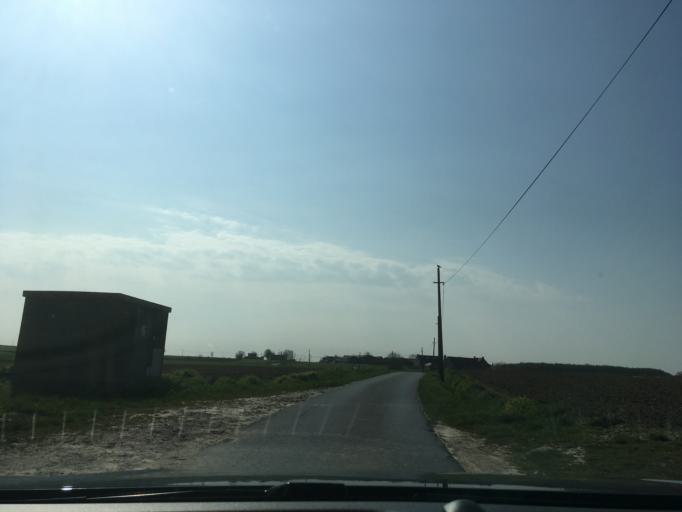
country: BE
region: Flanders
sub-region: Provincie West-Vlaanderen
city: Lichtervelde
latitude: 51.0087
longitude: 3.1611
